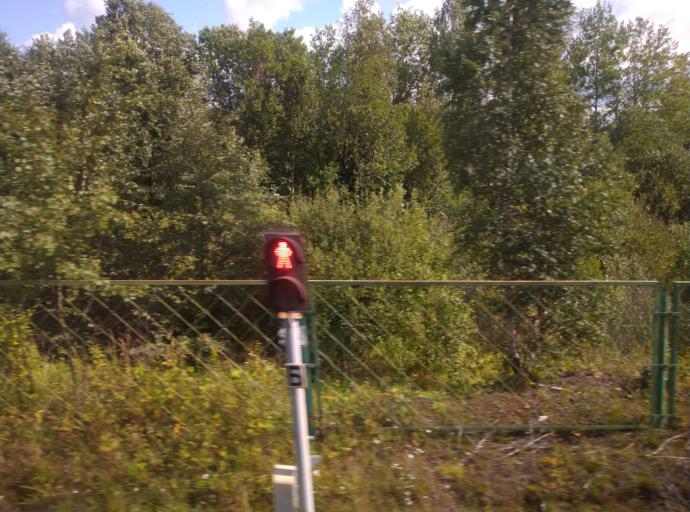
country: RU
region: Leningrad
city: Krasnyy Bor
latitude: 59.6785
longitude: 30.7039
